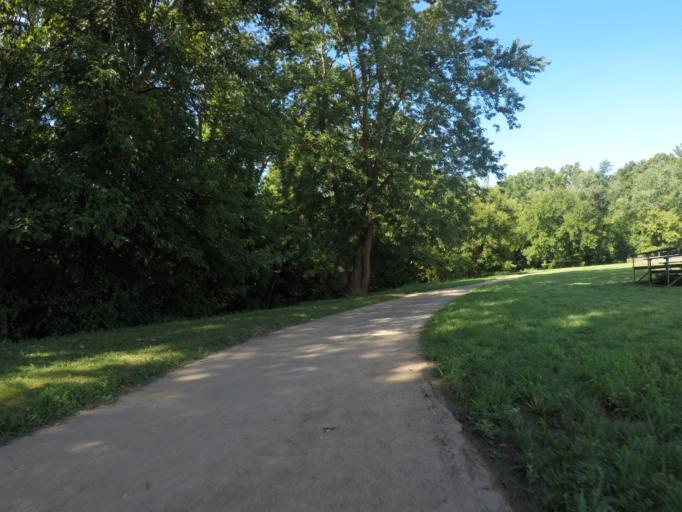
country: US
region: West Virginia
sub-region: Cabell County
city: Huntington
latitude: 38.4030
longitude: -82.4856
